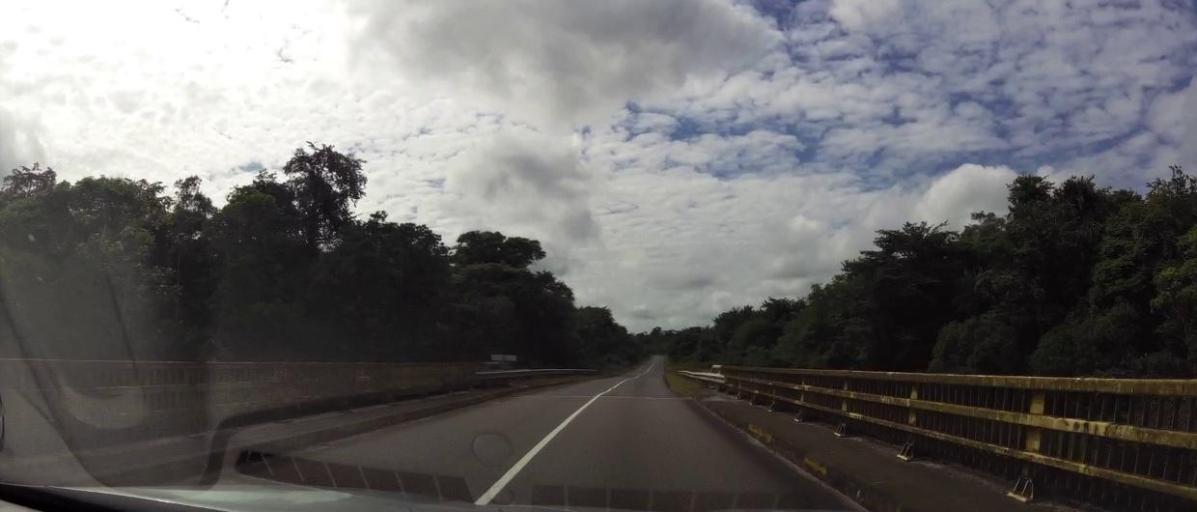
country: GF
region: Guyane
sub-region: Guyane
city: Sinnamary
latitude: 5.3730
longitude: -52.9662
